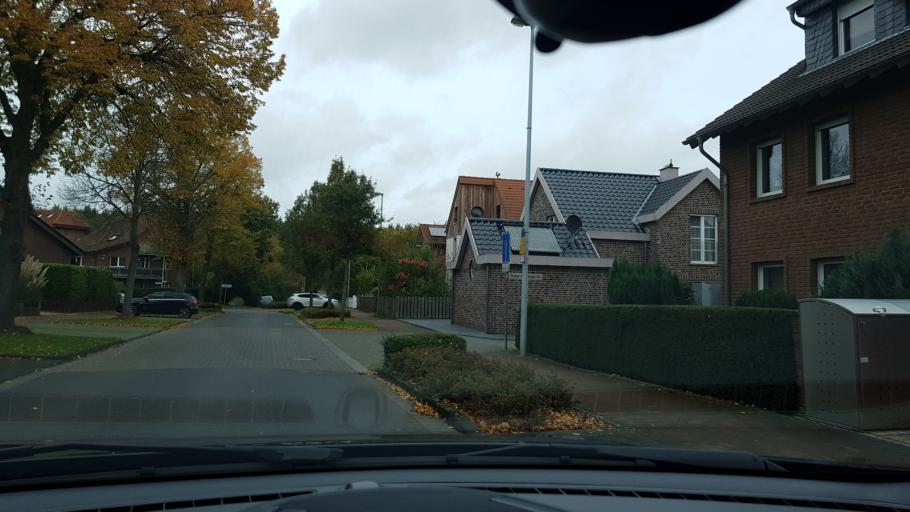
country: DE
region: North Rhine-Westphalia
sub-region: Regierungsbezirk Koln
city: Bedburg
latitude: 51.0088
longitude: 6.5481
